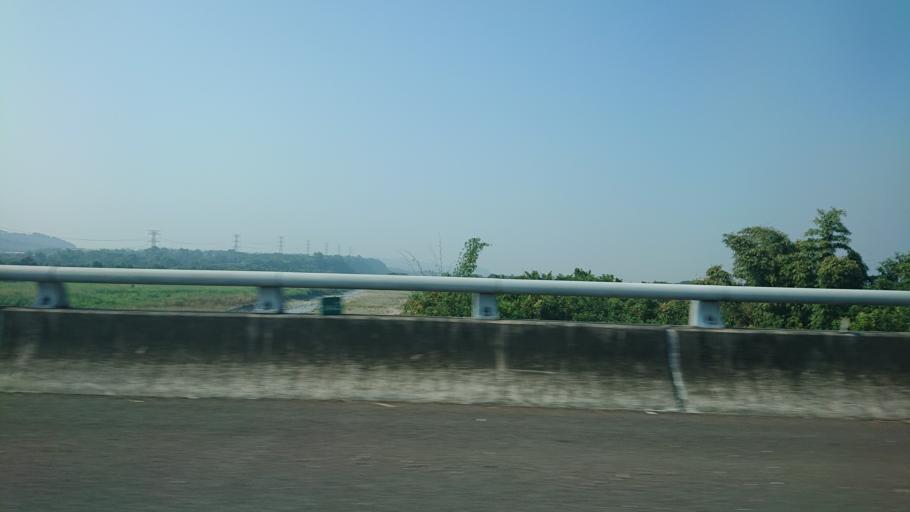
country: TW
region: Taiwan
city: Lugu
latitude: 23.7924
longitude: 120.7035
